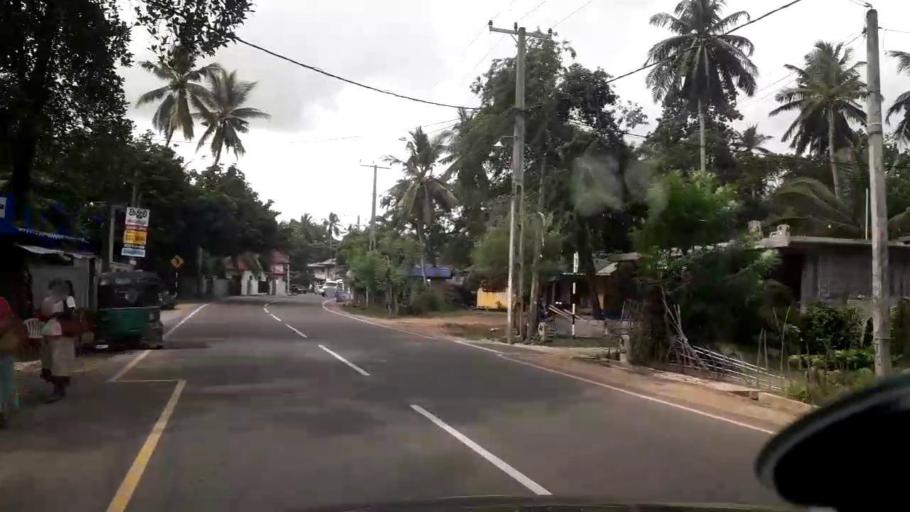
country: LK
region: Western
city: Panadura
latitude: 6.6672
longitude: 79.9369
